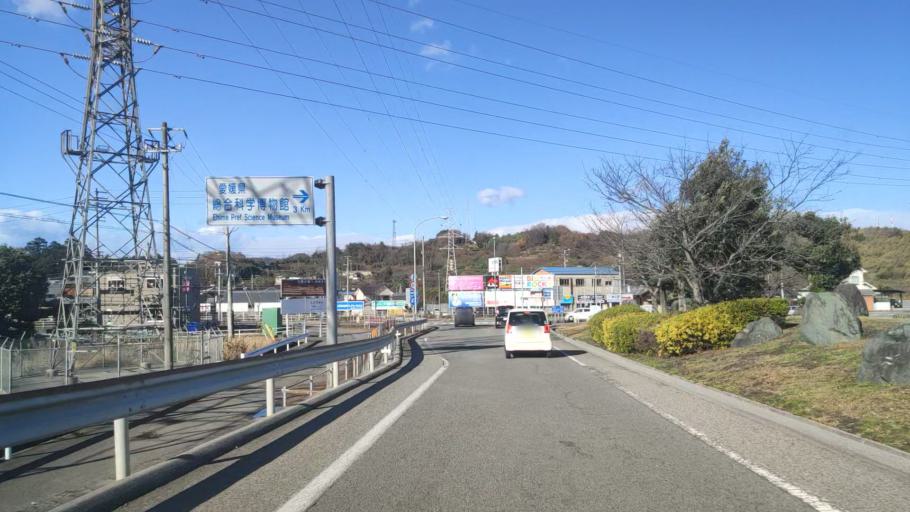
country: JP
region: Ehime
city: Saijo
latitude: 33.9189
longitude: 133.2403
